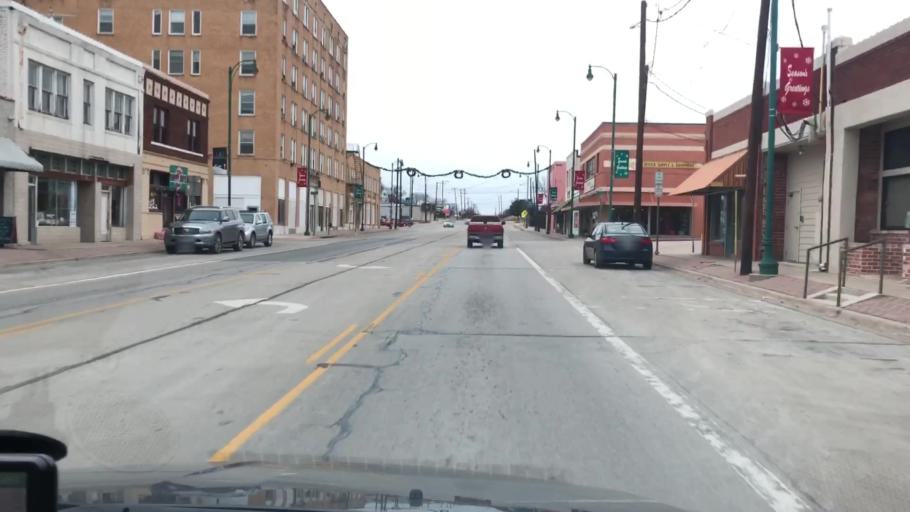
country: US
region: Texas
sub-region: Palo Pinto County
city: Mineral Wells
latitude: 32.8112
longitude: -98.1128
